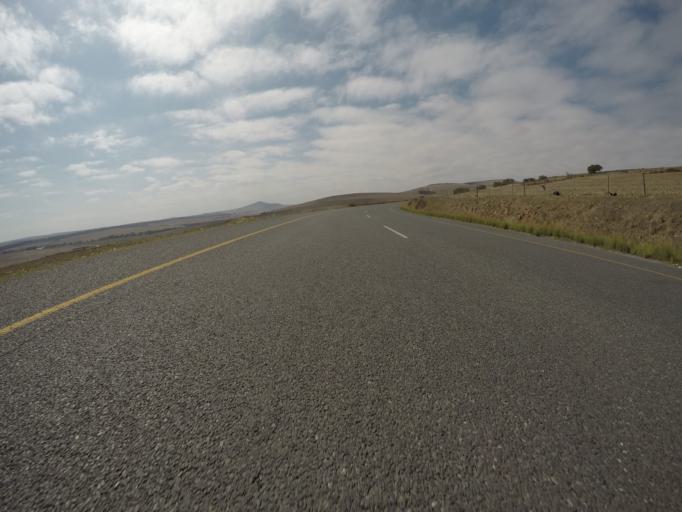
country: ZA
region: Western Cape
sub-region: City of Cape Town
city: Sunset Beach
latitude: -33.7917
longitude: 18.5712
